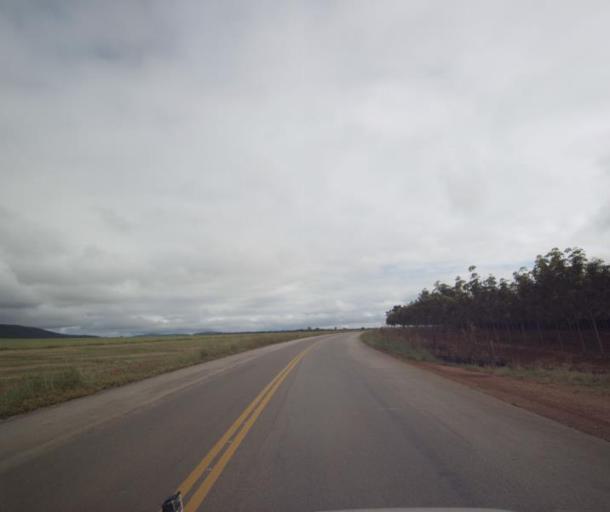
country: BR
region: Goias
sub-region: Padre Bernardo
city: Padre Bernardo
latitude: -15.3795
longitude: -48.6449
